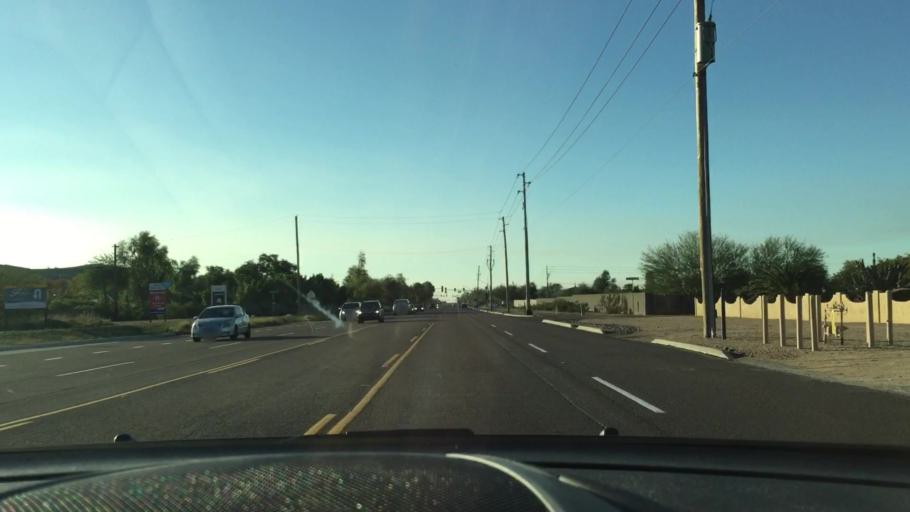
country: US
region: Arizona
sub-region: Maricopa County
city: Sun City
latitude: 33.6986
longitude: -112.2031
